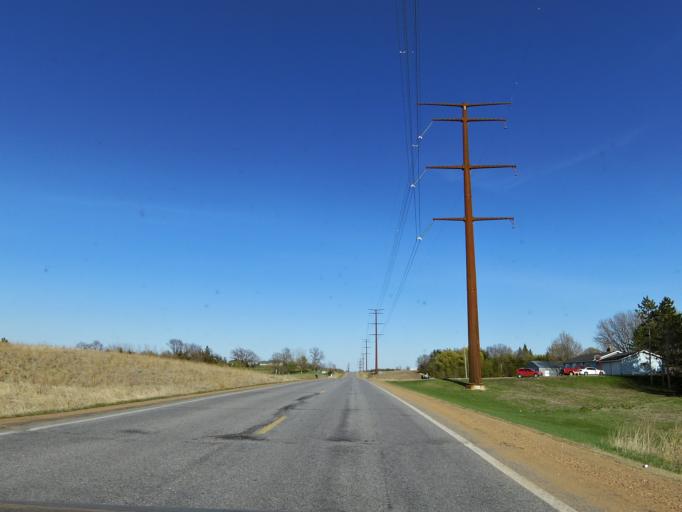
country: US
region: Minnesota
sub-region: Le Sueur County
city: New Prague
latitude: 44.5725
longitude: -93.4847
